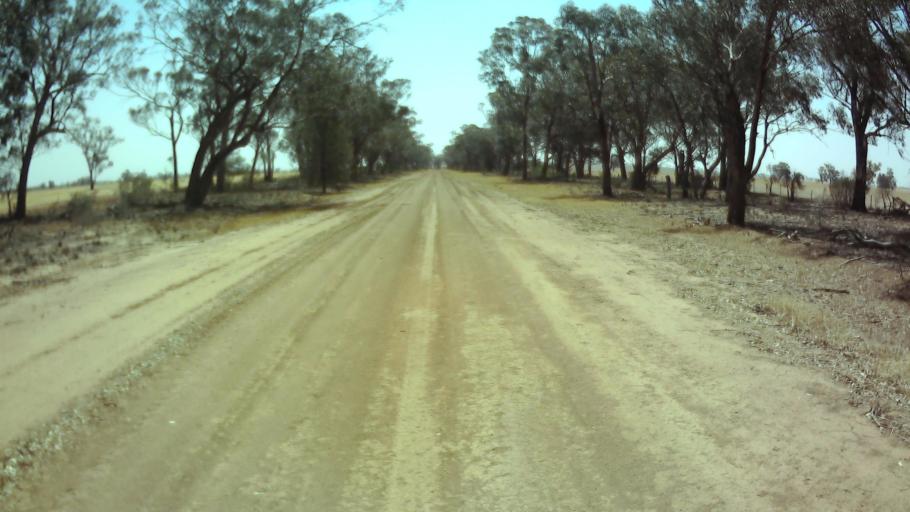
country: AU
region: New South Wales
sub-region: Weddin
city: Grenfell
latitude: -33.9252
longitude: 147.7876
